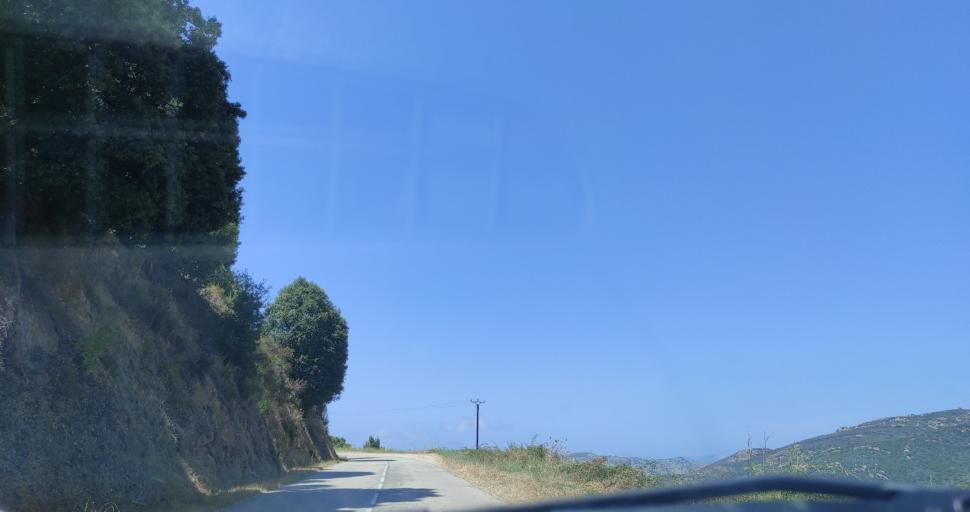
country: FR
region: Corsica
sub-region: Departement de la Corse-du-Sud
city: Alata
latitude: 41.9684
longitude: 8.7083
